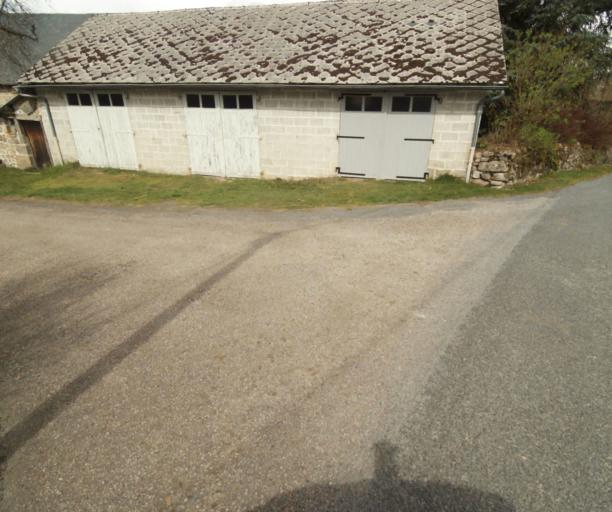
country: FR
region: Limousin
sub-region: Departement de la Correze
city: Correze
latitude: 45.3300
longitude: 1.9529
